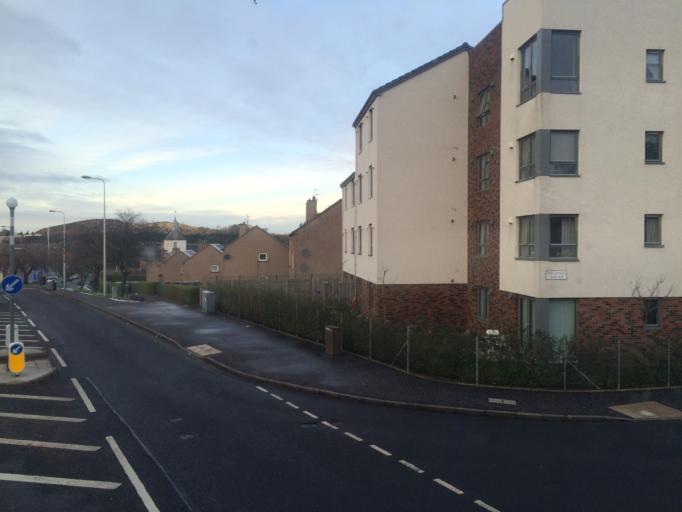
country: GB
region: Scotland
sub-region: Edinburgh
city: Colinton
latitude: 55.9074
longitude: -3.2270
